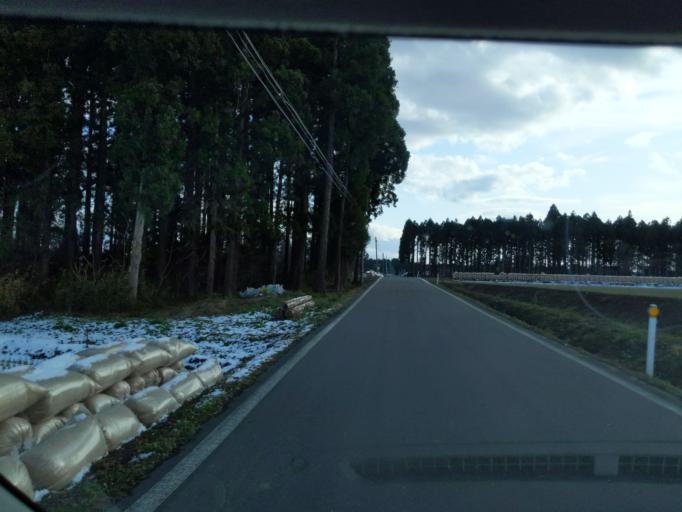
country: JP
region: Iwate
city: Mizusawa
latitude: 39.1238
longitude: 141.0816
